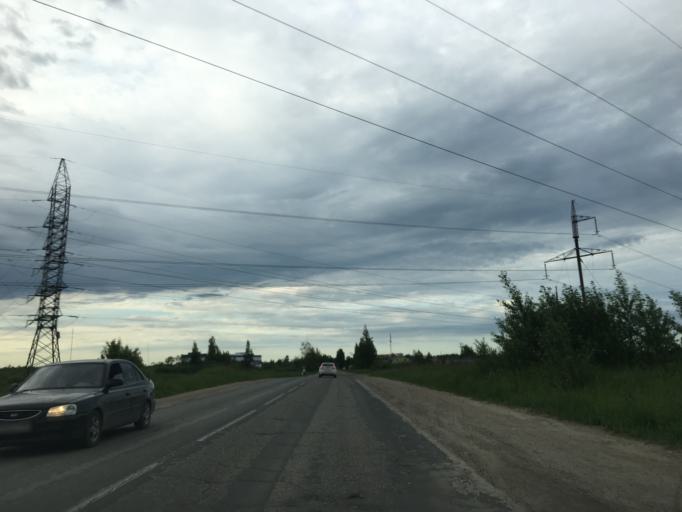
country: RU
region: Pskov
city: Pskov
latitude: 57.8459
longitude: 28.3063
